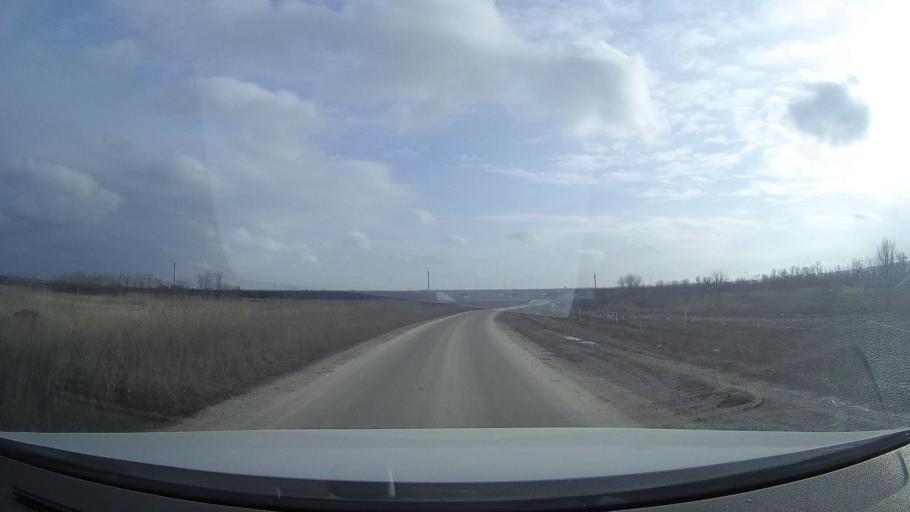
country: RU
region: Rostov
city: Grushevskaya
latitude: 47.4561
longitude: 39.8792
